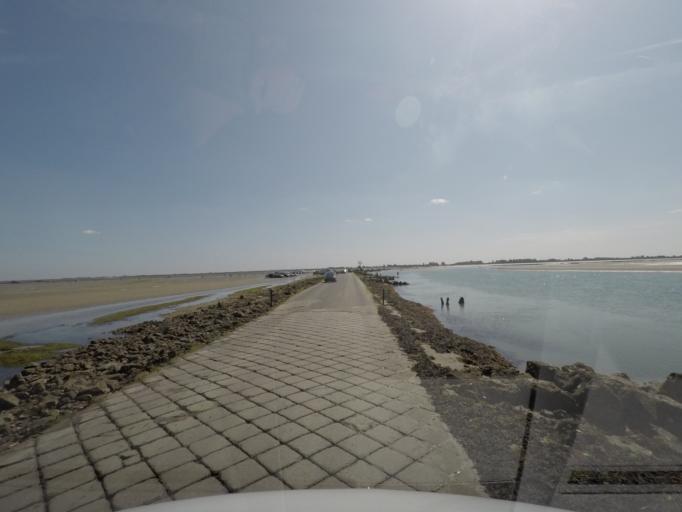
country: FR
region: Pays de la Loire
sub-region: Departement de la Vendee
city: La Barre-de-Monts
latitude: 46.9287
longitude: -2.1177
